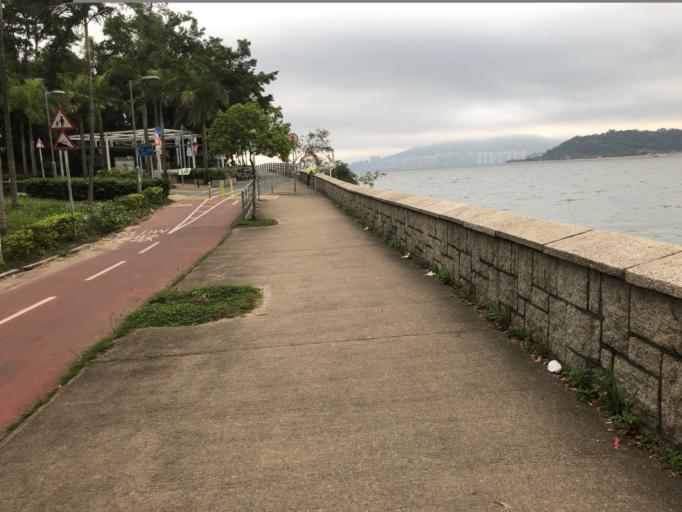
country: HK
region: Tai Po
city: Tai Po
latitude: 22.4495
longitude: 114.1772
